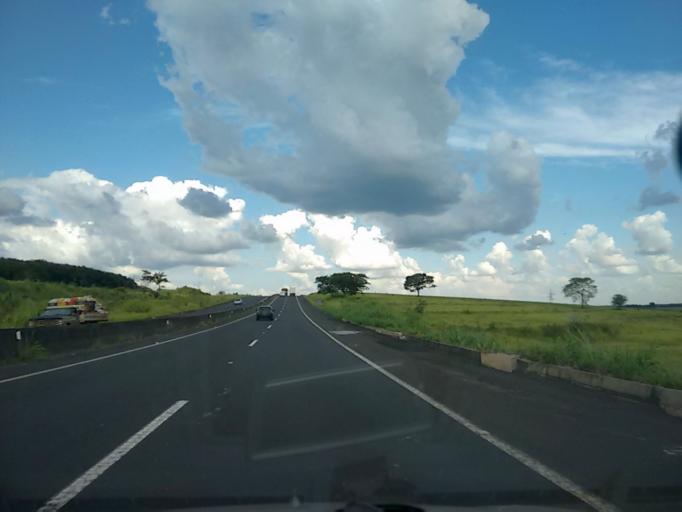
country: BR
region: Sao Paulo
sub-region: Garca
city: Garca
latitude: -22.2265
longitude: -49.7917
